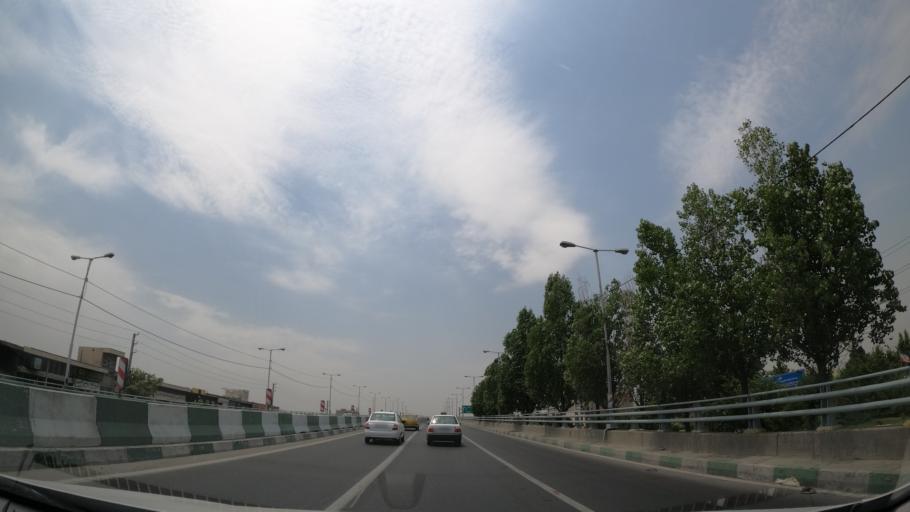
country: IR
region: Tehran
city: Eslamshahr
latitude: 35.6767
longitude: 51.2811
